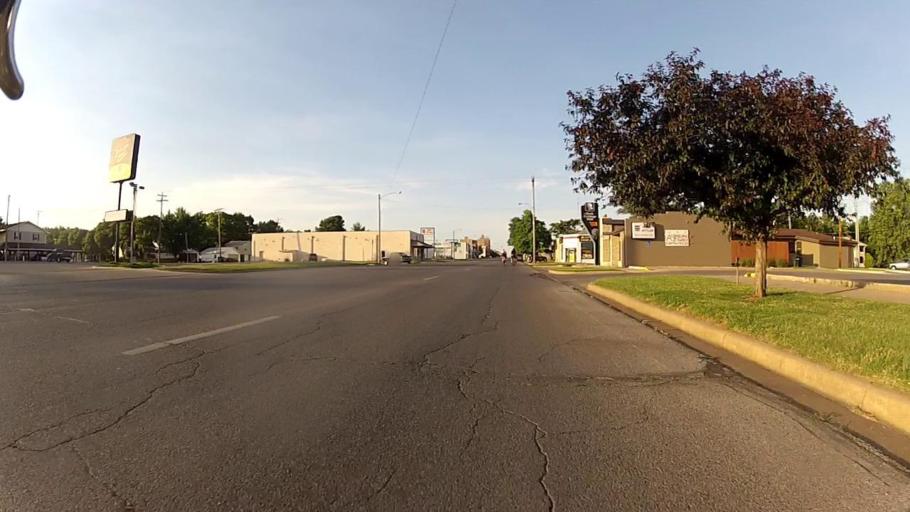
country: US
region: Kansas
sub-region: Cowley County
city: Arkansas City
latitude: 37.0665
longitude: -97.0392
